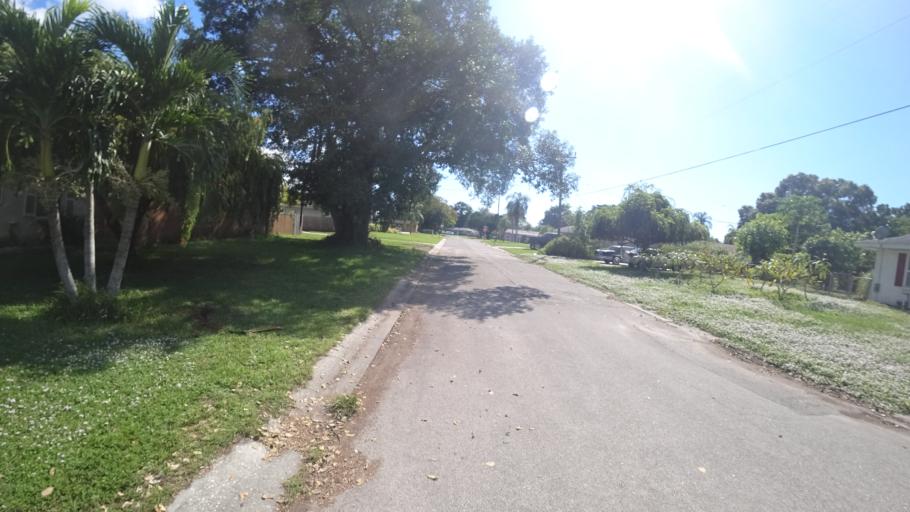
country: US
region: Florida
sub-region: Manatee County
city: South Bradenton
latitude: 27.4799
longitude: -82.5856
